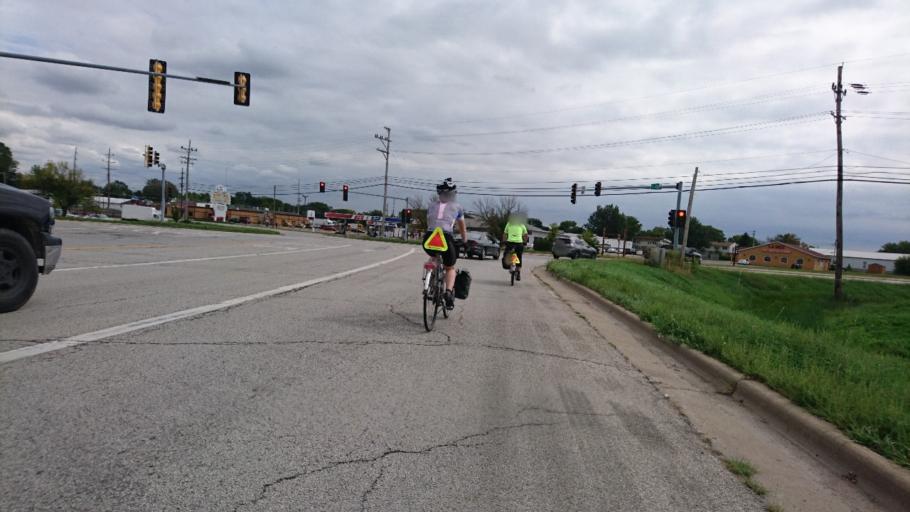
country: US
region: Illinois
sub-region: Livingston County
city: Pontiac
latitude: 40.8869
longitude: -88.6426
